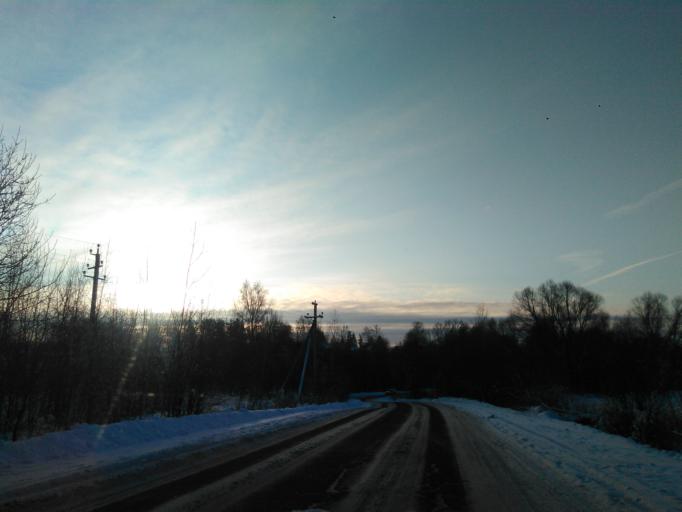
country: RU
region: Tverskaya
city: Zavidovo
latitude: 56.6143
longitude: 36.6185
